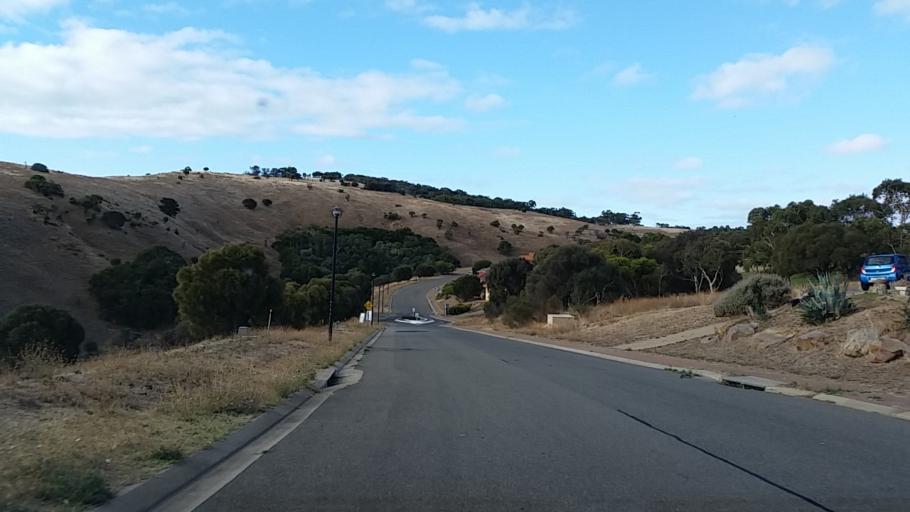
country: AU
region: South Australia
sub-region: Yankalilla
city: Normanville
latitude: -35.5024
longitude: 138.2496
